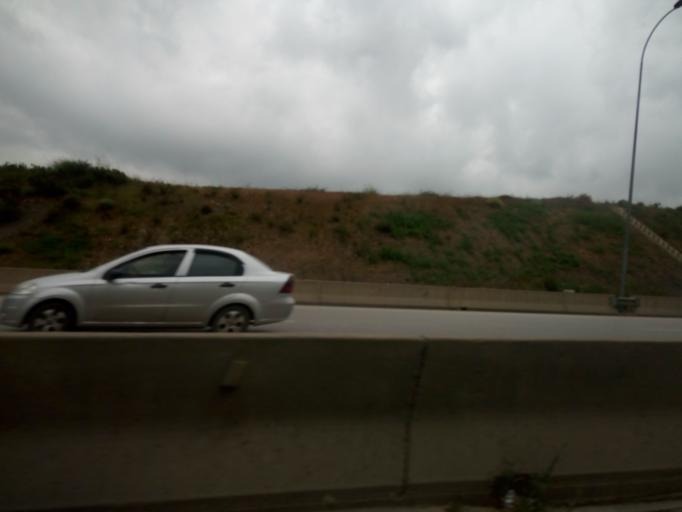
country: DZ
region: Bouira
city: Lakhdaria
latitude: 36.5876
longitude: 3.5295
